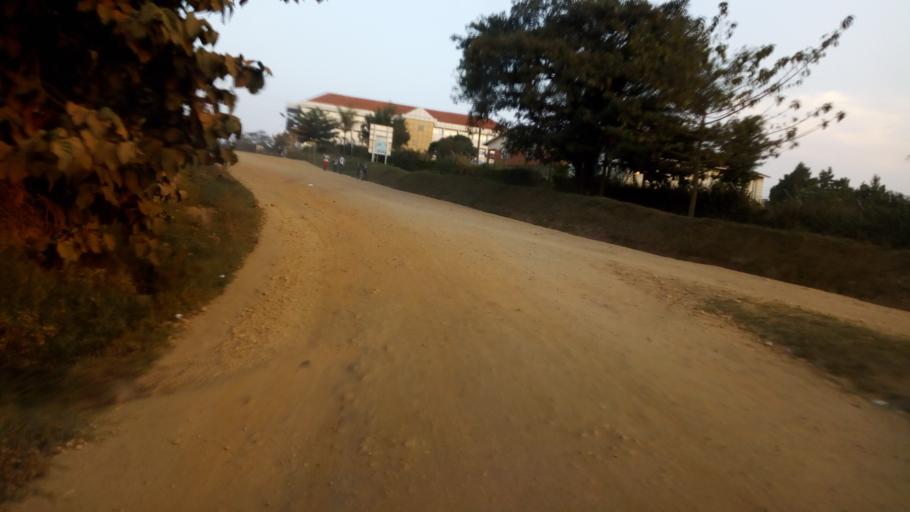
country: UG
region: Western Region
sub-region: Rukungiri District
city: Rukungiri
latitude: -0.7830
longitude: 29.9255
